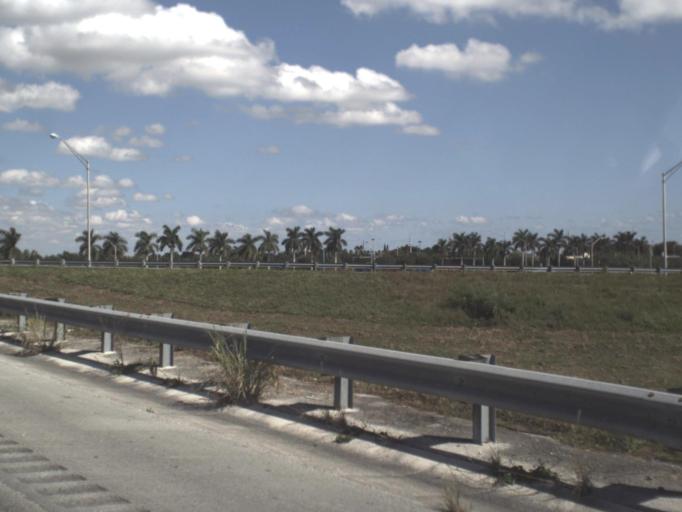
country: US
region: Florida
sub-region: Miami-Dade County
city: Leisure City
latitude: 25.4977
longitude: -80.4174
